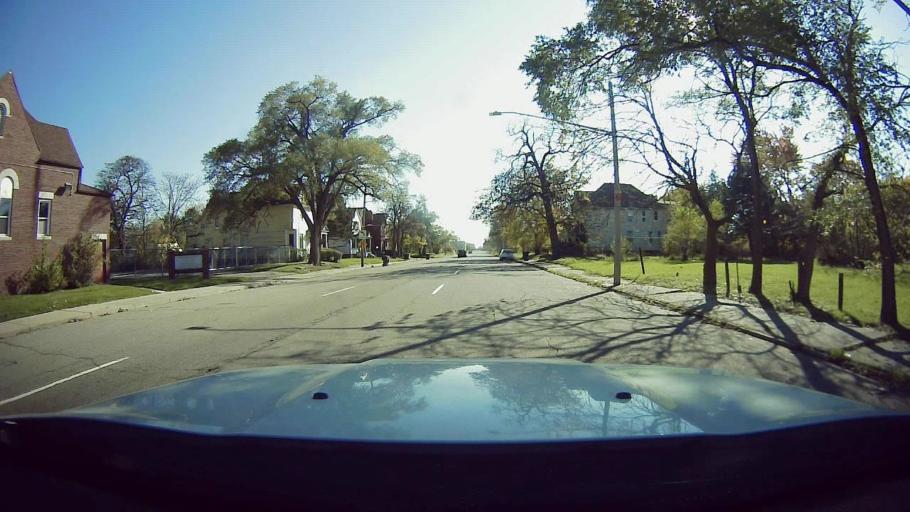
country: US
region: Michigan
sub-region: Wayne County
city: Highland Park
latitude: 42.3567
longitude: -83.0909
